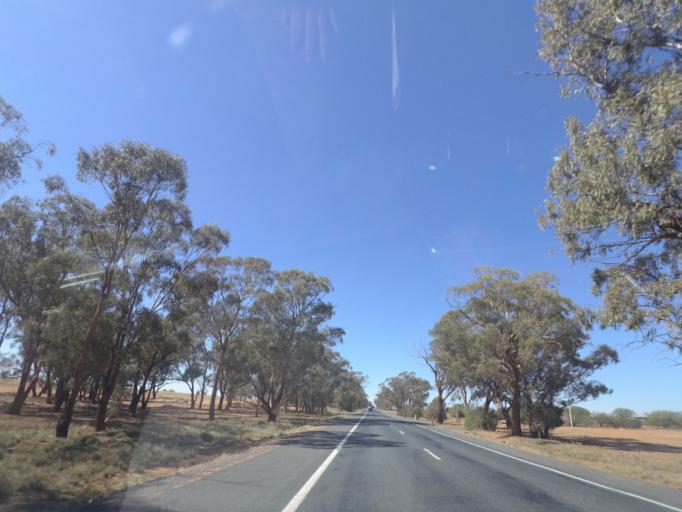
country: AU
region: New South Wales
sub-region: Bland
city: West Wyalong
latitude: -34.2058
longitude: 147.1096
